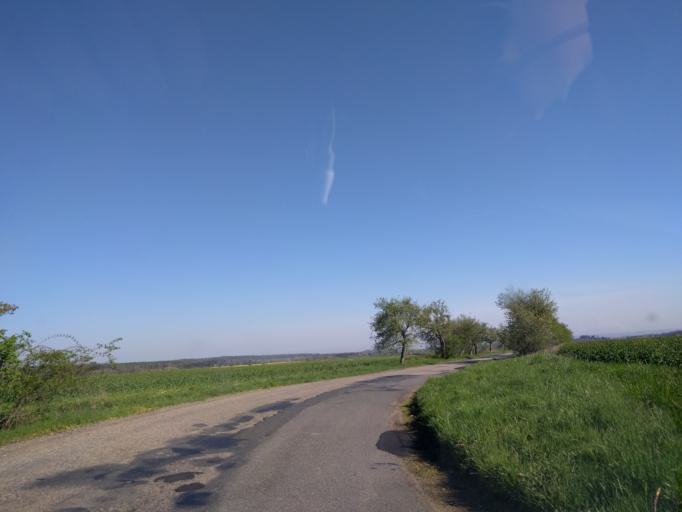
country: CZ
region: Central Bohemia
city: Mukarov
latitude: 49.9957
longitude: 14.7738
